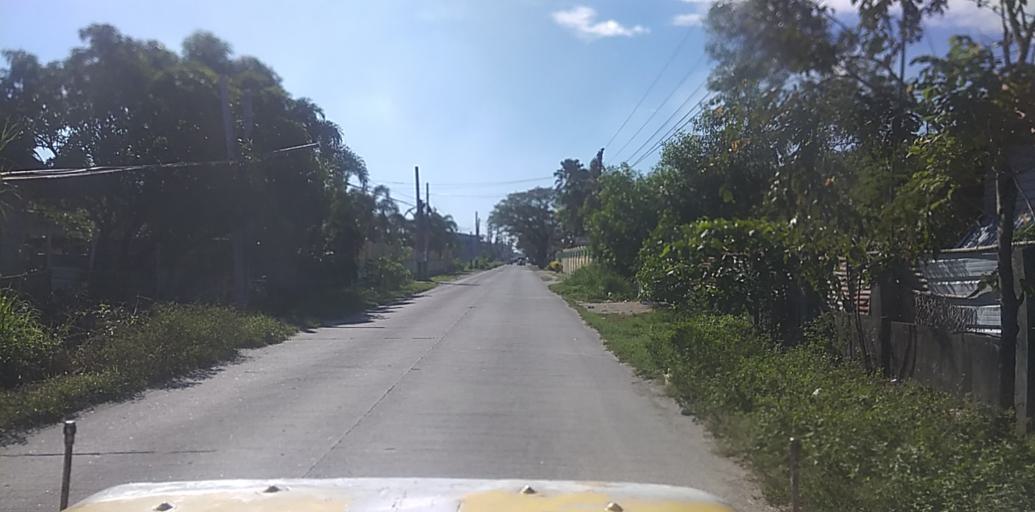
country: PH
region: Central Luzon
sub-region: Province of Pampanga
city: Mexico
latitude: 15.0761
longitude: 120.7187
